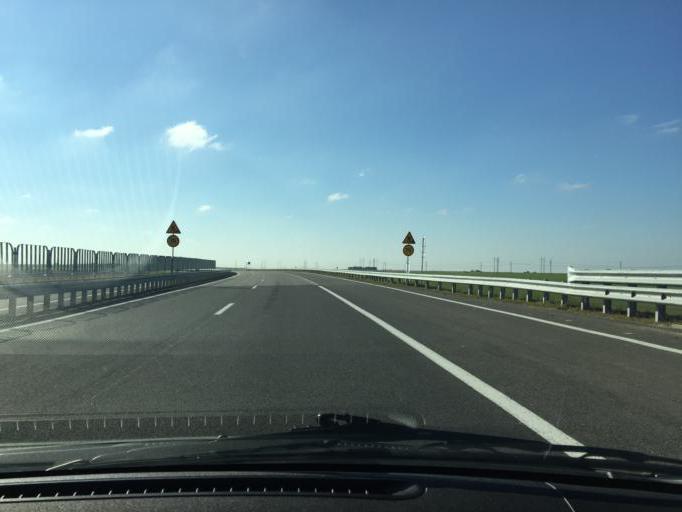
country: BY
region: Minsk
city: Slutsk
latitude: 53.0447
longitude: 27.4948
